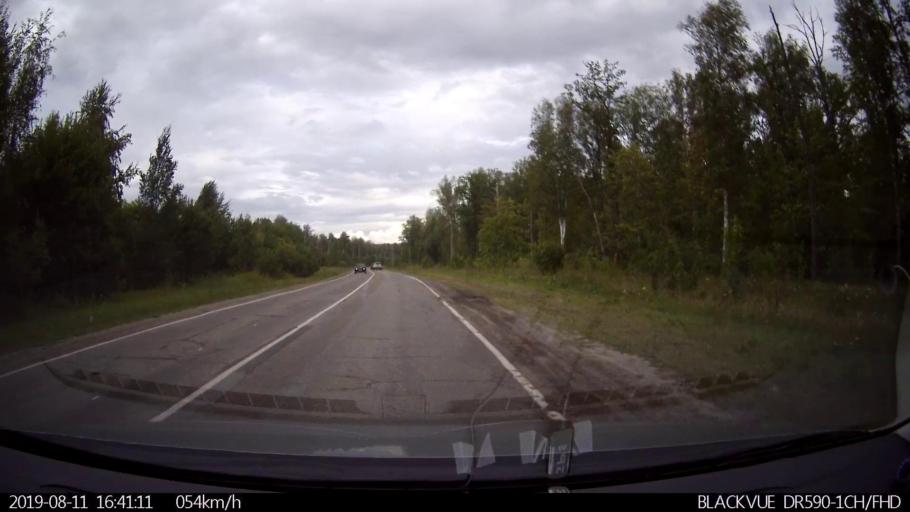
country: RU
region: Ulyanovsk
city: Mayna
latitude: 54.1514
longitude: 47.6511
